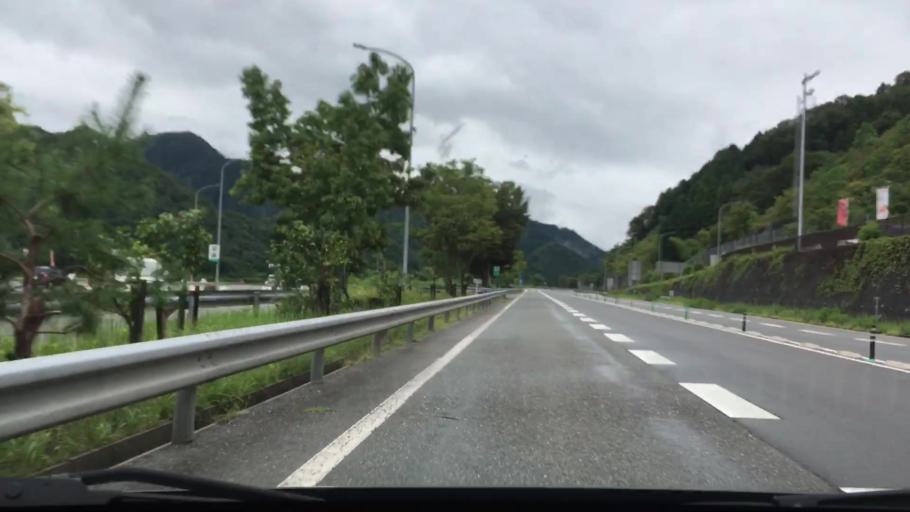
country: JP
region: Hyogo
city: Nishiwaki
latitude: 35.2133
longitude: 134.7939
